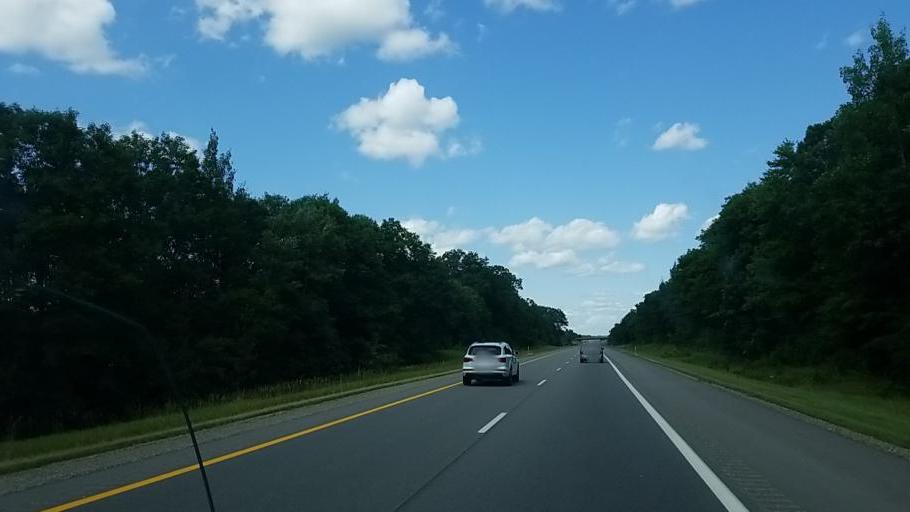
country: US
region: Michigan
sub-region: Montcalm County
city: Howard City
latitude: 43.4486
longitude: -85.4865
